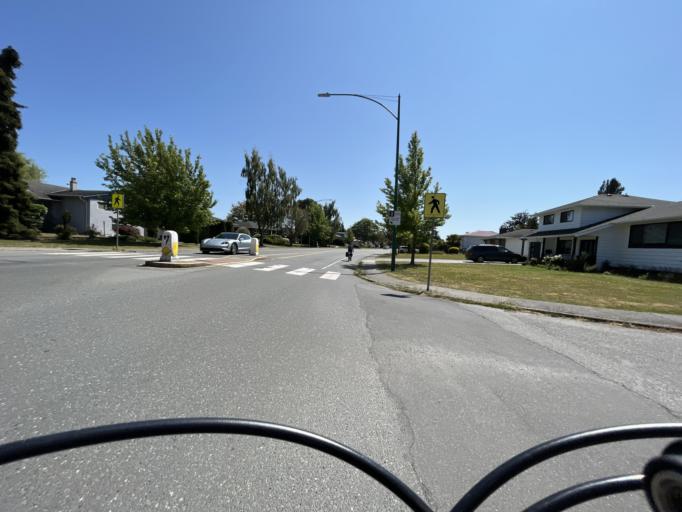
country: CA
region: British Columbia
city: Oak Bay
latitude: 48.4551
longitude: -123.3144
